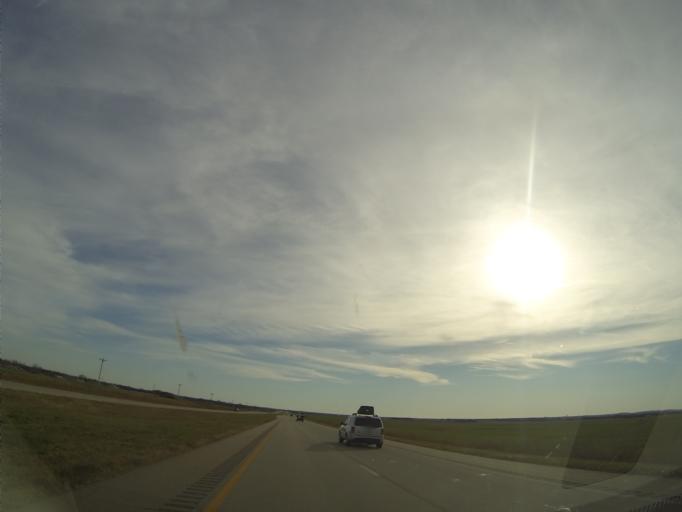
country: US
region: Kansas
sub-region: Ottawa County
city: Minneapolis
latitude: 39.1676
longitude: -97.6685
